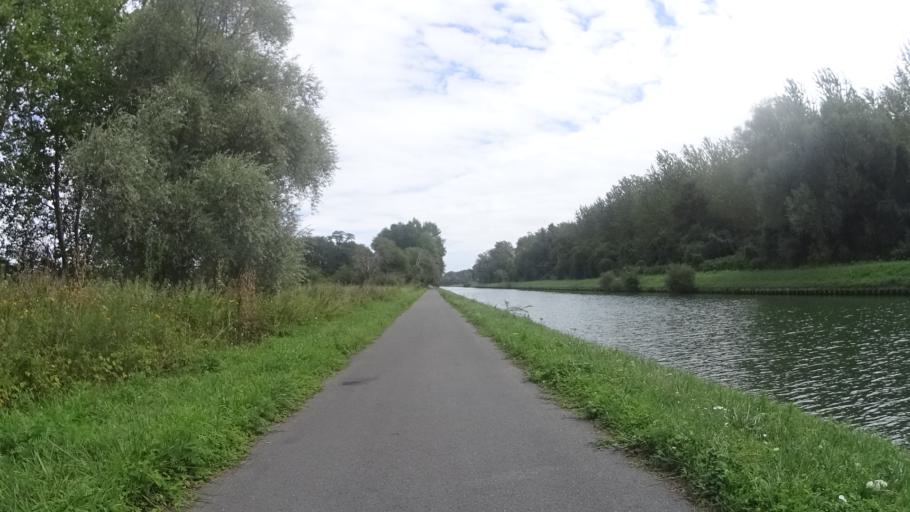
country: FR
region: Picardie
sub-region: Departement de l'Oise
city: Crisolles
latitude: 49.5779
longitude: 3.0750
